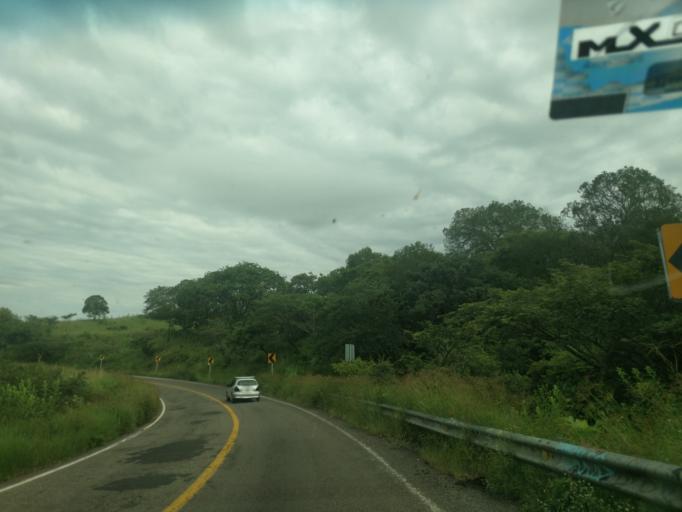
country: MX
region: Jalisco
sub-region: Atengo
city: Soyatlan del Oro
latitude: 20.5449
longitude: -104.2920
